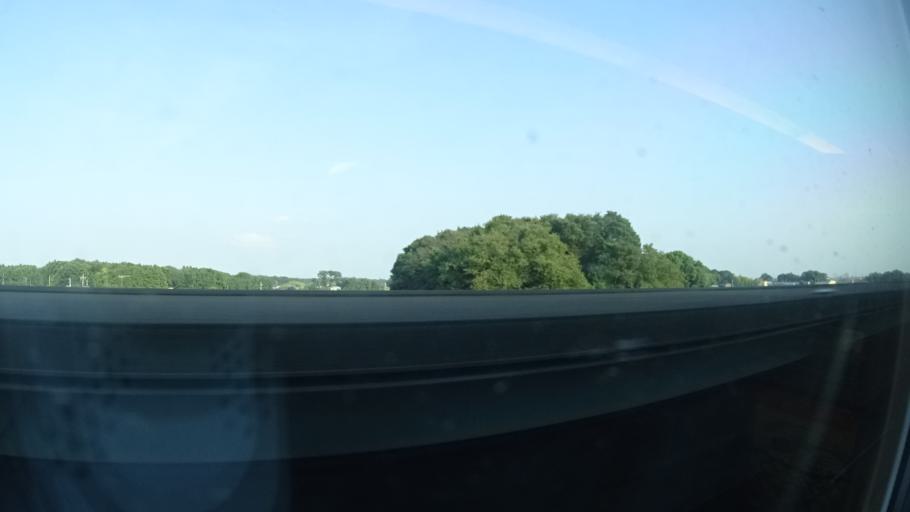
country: JP
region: Ibaraki
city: Koga
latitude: 36.2215
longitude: 139.7555
